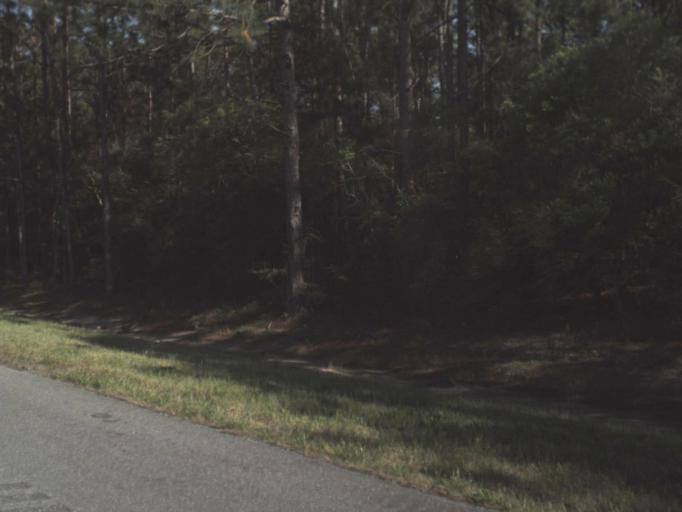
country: US
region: Florida
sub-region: Okaloosa County
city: Crestview
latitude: 30.7166
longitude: -86.6554
